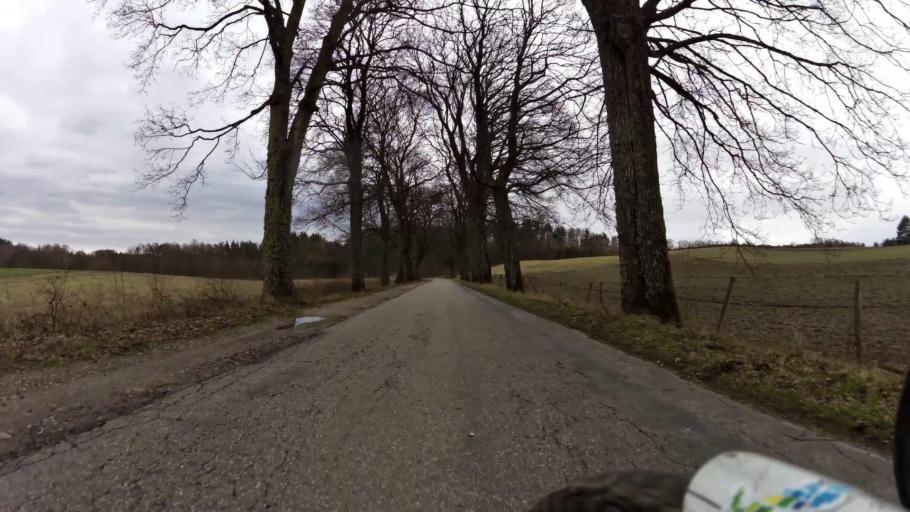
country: PL
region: Pomeranian Voivodeship
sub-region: Powiat bytowski
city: Trzebielino
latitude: 54.1000
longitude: 17.1320
